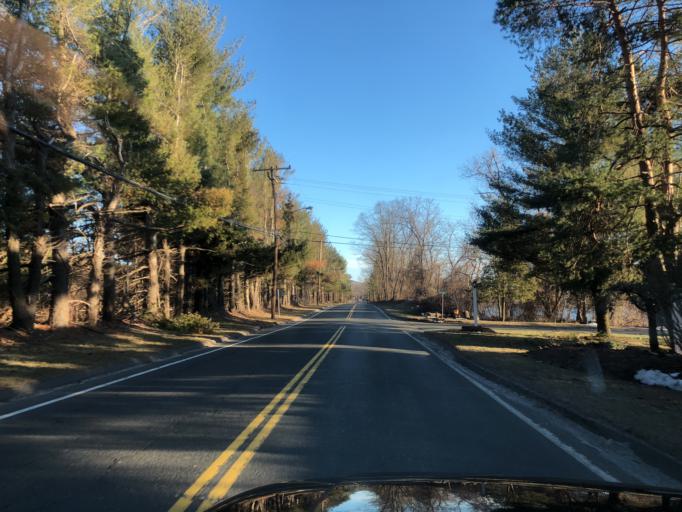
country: US
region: Connecticut
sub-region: Hartford County
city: Farmington
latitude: 41.7463
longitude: -72.8542
